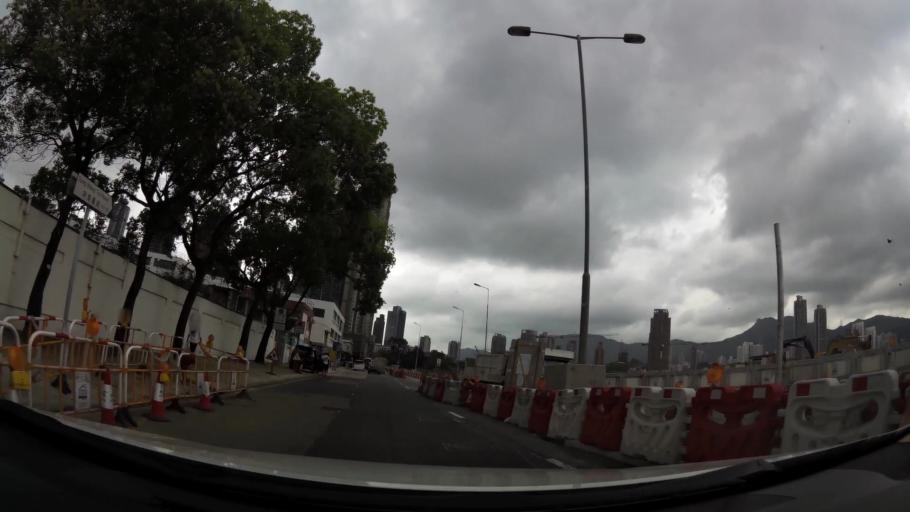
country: HK
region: Kowloon City
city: Kowloon
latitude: 22.3222
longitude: 114.1943
